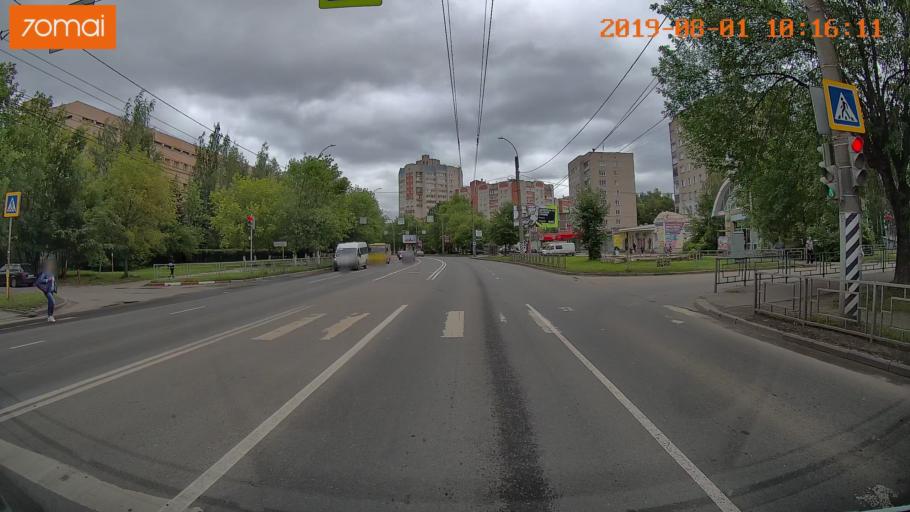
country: RU
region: Ivanovo
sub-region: Gorod Ivanovo
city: Ivanovo
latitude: 56.9632
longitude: 40.9953
